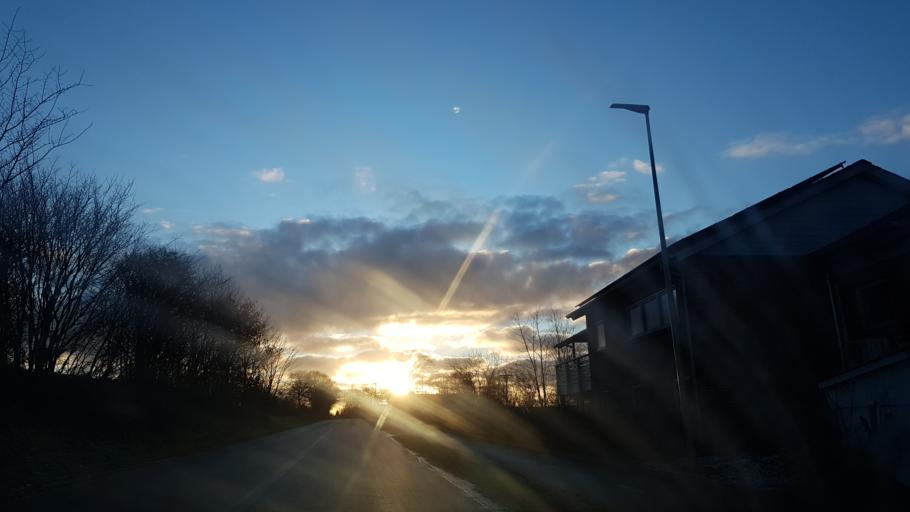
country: DK
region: South Denmark
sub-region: Kolding Kommune
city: Vamdrup
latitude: 55.3965
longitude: 9.3699
